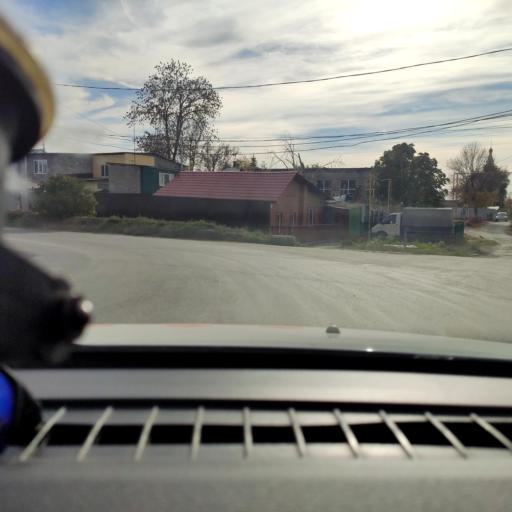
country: RU
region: Samara
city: Samara
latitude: 53.1824
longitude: 50.1337
